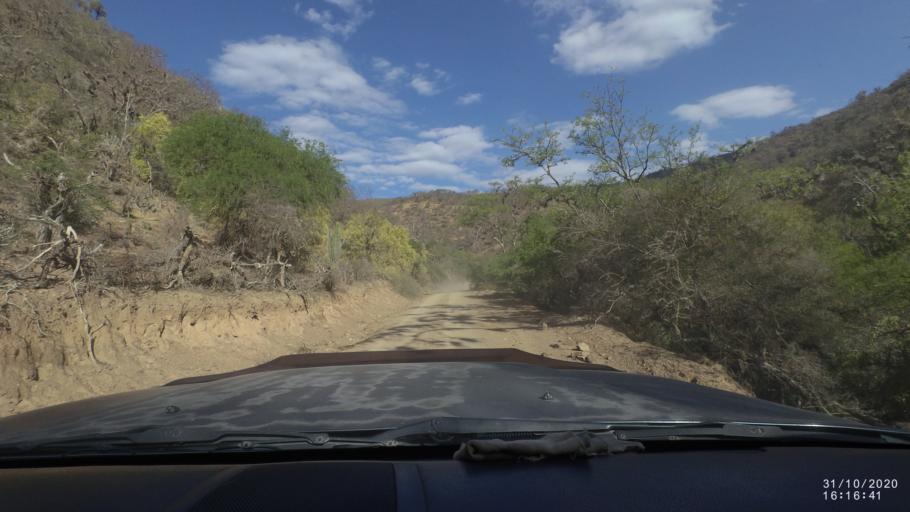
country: BO
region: Chuquisaca
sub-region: Provincia Zudanez
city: Mojocoya
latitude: -18.3900
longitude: -64.6080
